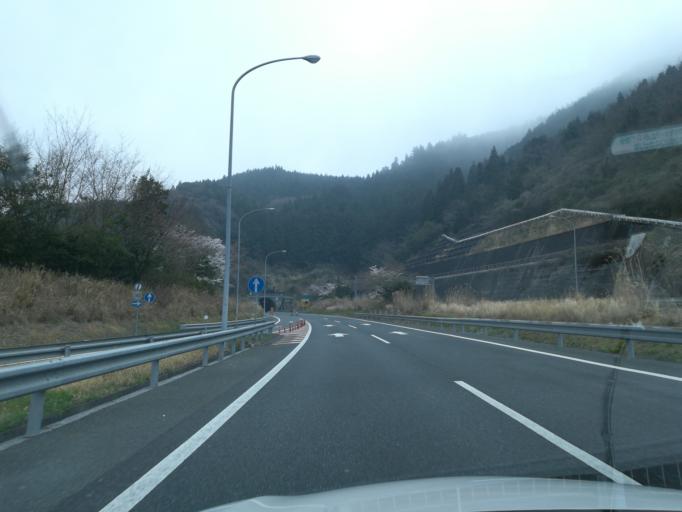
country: JP
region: Kochi
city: Kochi-shi
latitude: 33.7715
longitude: 133.6600
